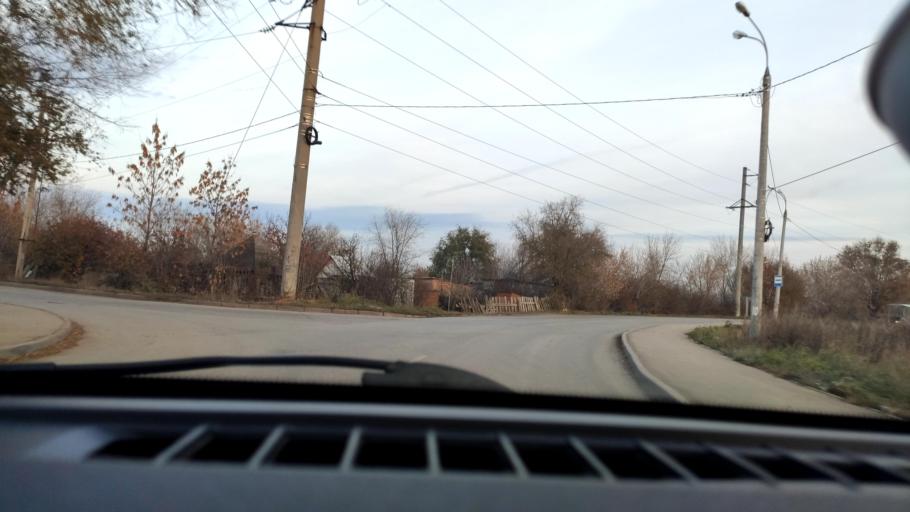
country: RU
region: Samara
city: Samara
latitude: 53.1472
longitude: 50.1395
